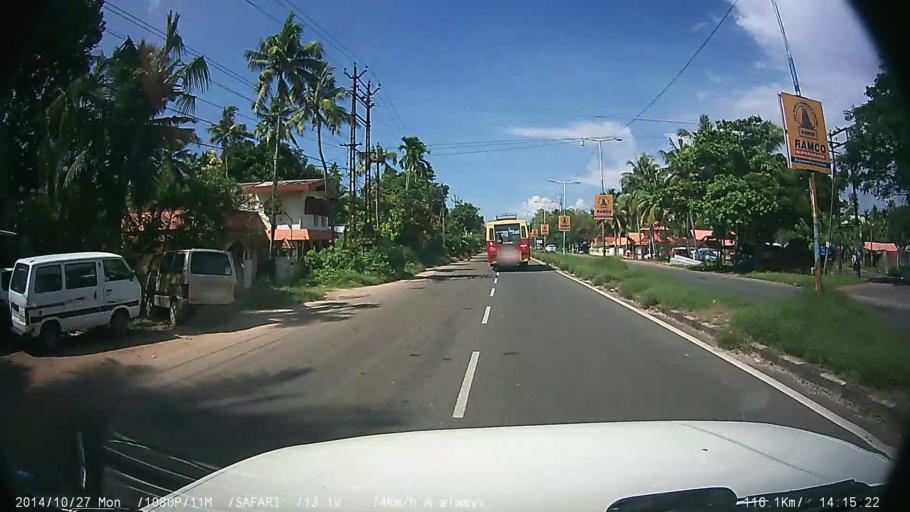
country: IN
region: Kerala
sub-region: Alappuzha
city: Kutiatodu
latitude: 9.8320
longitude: 76.3095
